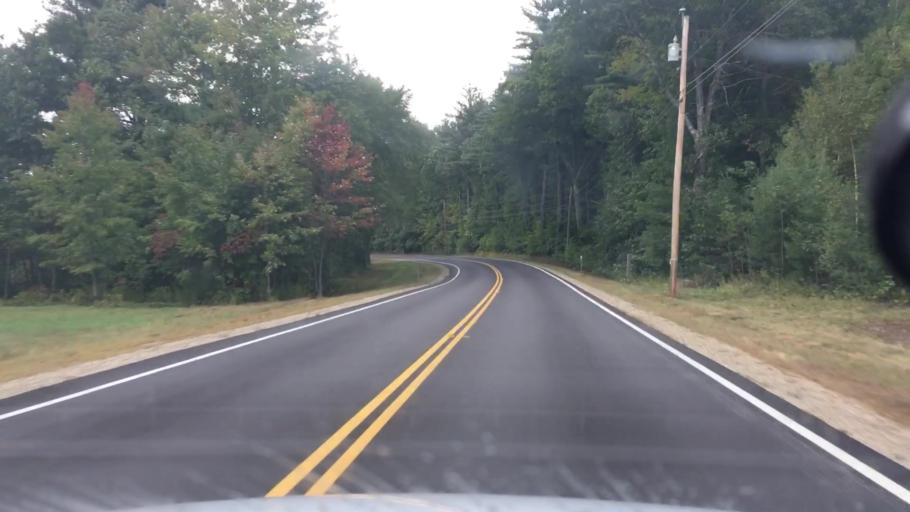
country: US
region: New Hampshire
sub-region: Carroll County
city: Sanbornville
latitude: 43.5308
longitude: -71.0227
